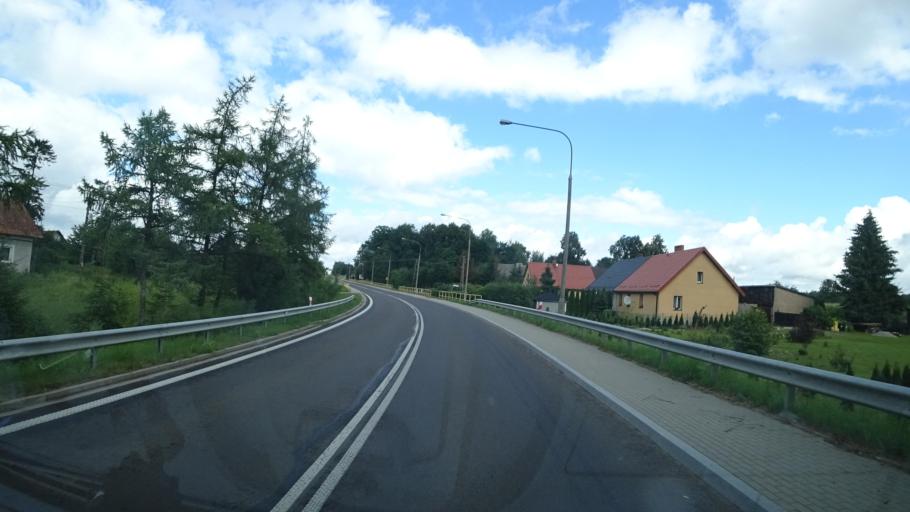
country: PL
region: Warmian-Masurian Voivodeship
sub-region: Powiat olecki
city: Kowale Oleckie
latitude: 54.2082
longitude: 22.4131
